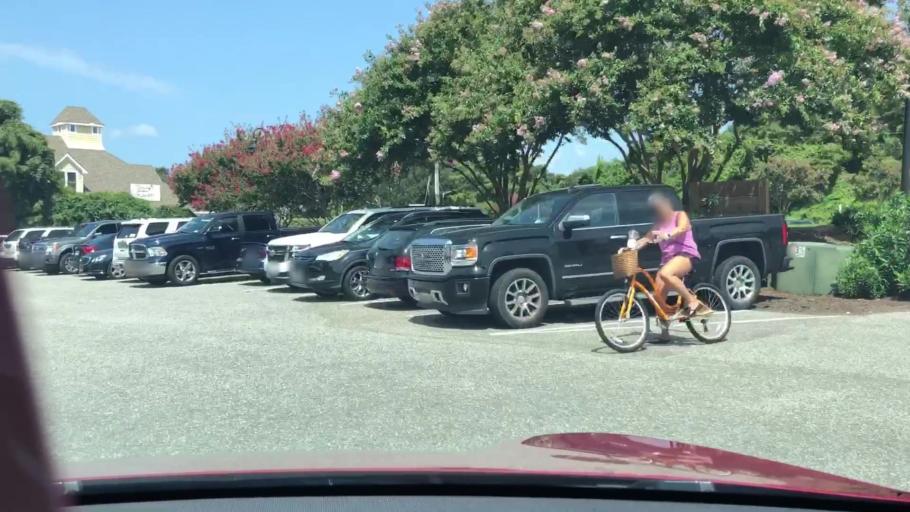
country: US
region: North Carolina
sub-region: Dare County
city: Southern Shores
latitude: 36.1701
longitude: -75.7567
